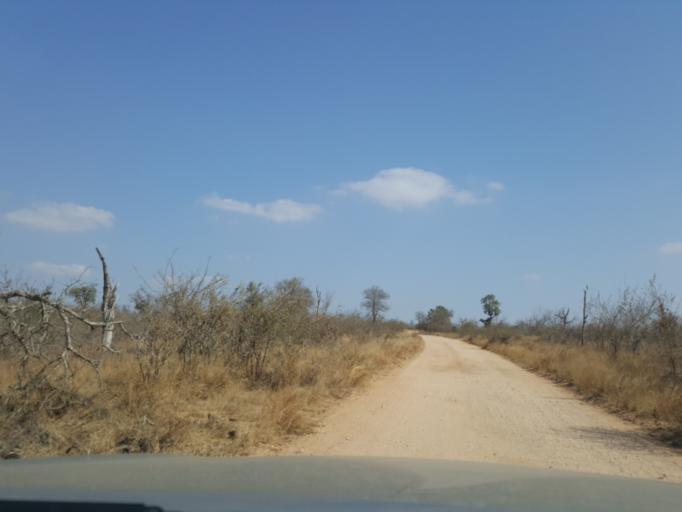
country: ZA
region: Mpumalanga
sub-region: Ehlanzeni District
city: Komatipoort
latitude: -25.3005
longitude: 31.7571
